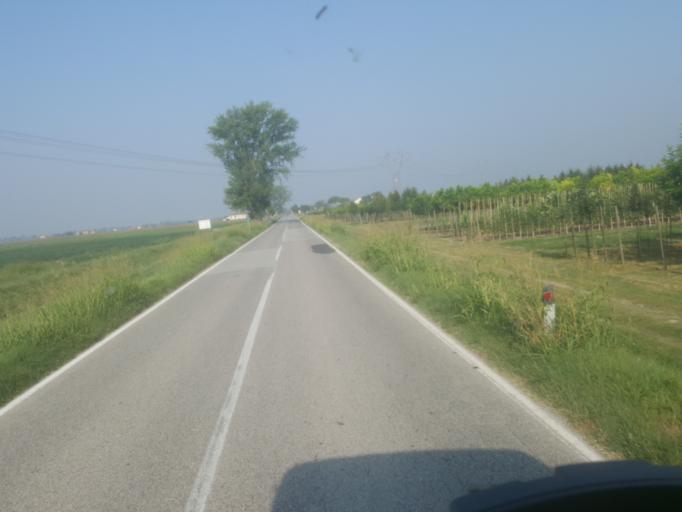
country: IT
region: Emilia-Romagna
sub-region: Provincia di Ravenna
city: Voltana
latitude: 44.5563
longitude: 11.9288
